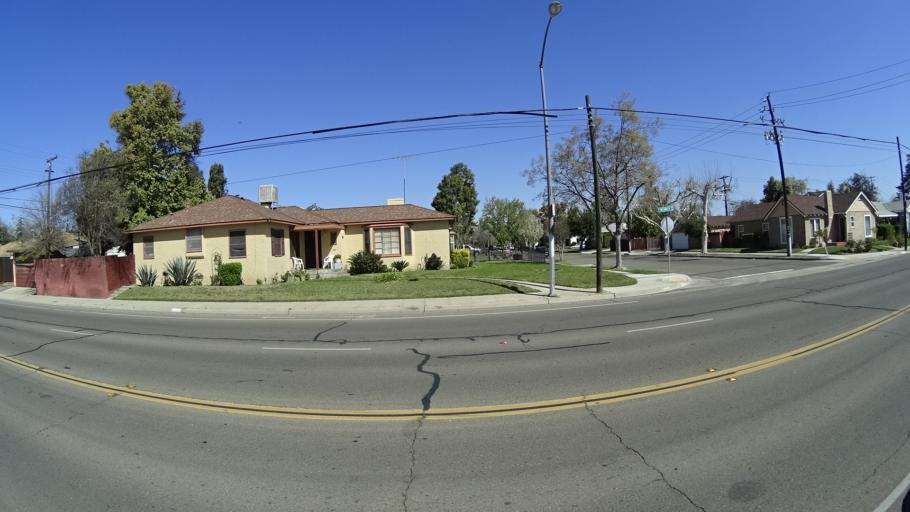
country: US
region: California
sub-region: Fresno County
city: Fresno
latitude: 36.7648
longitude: -119.8111
